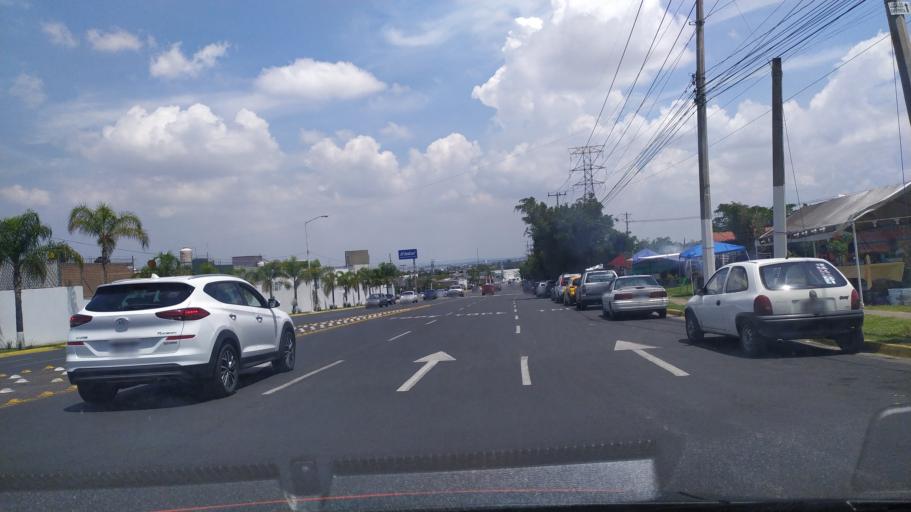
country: MX
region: Jalisco
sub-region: Zapopan
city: Zapopan
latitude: 20.7559
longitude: -103.3865
